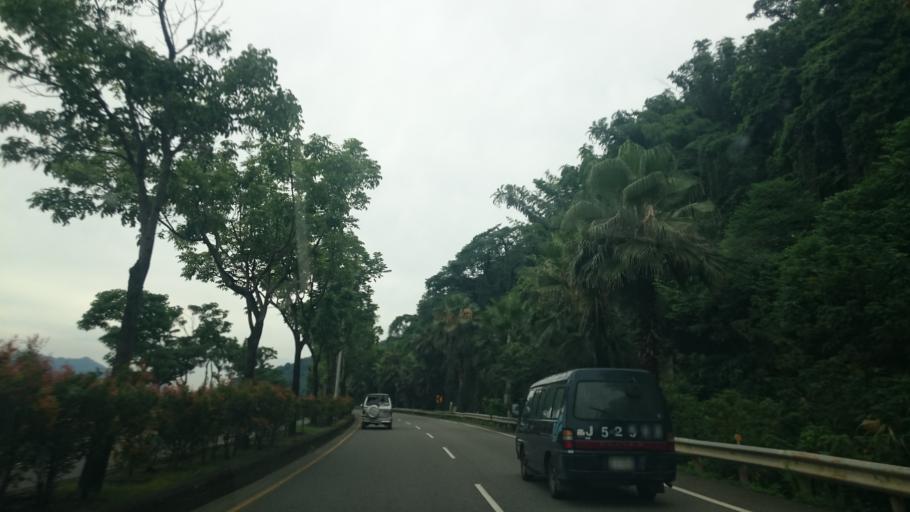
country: TW
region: Taiwan
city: Lugu
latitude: 23.8226
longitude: 120.8372
